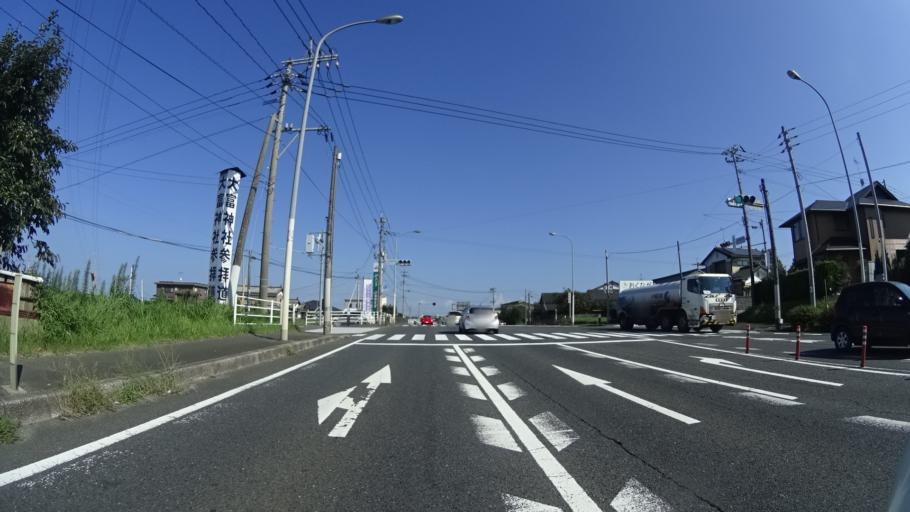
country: JP
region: Fukuoka
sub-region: Buzen-shi
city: Buzen
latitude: 33.6127
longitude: 131.1031
